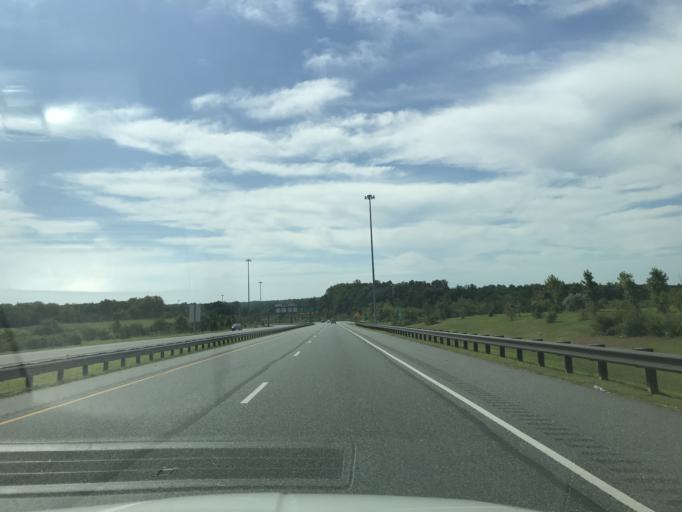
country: US
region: Maryland
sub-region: Prince George's County
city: West Laurel
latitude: 39.0716
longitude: -76.9037
